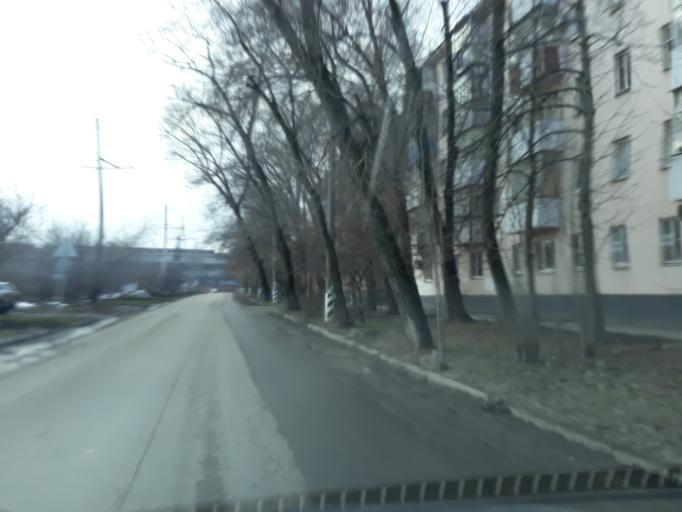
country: RU
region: Rostov
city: Taganrog
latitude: 47.2502
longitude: 38.9085
